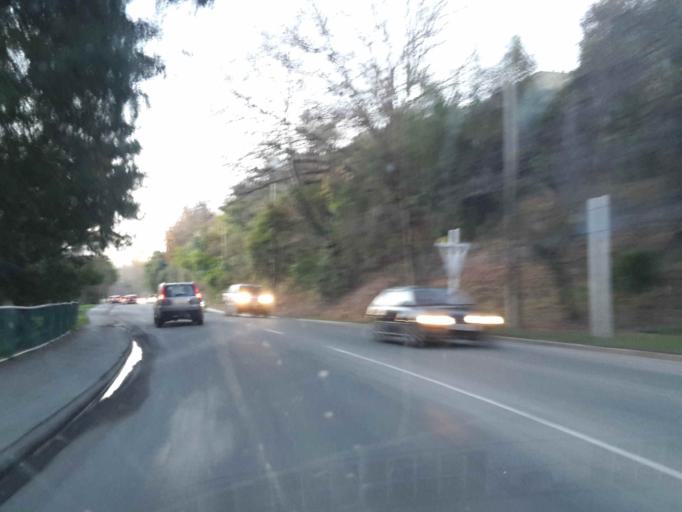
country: NZ
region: Canterbury
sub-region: Christchurch City
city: Christchurch
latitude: -43.5736
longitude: 172.6173
